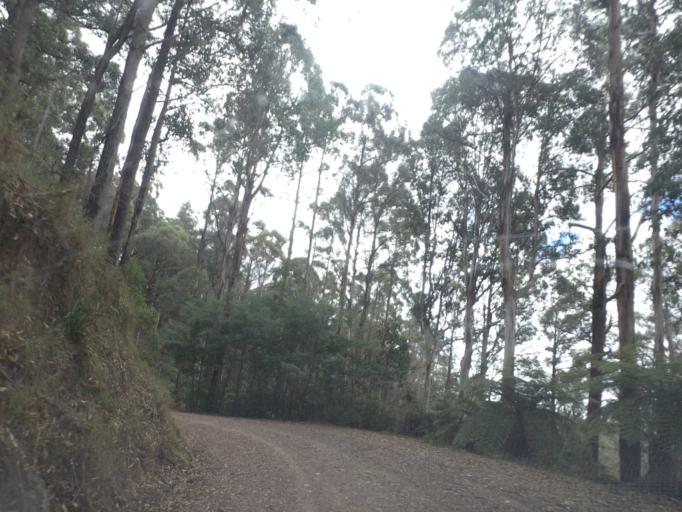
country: AU
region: Victoria
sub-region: Murrindindi
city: Alexandra
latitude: -37.4561
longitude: 145.9670
